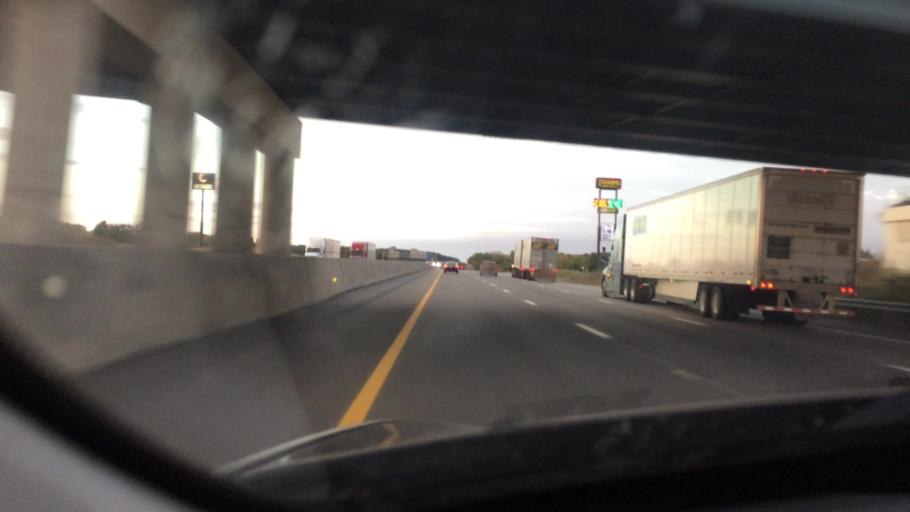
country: US
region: Ohio
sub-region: Wood County
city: North Baltimore
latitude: 41.1380
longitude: -83.6591
